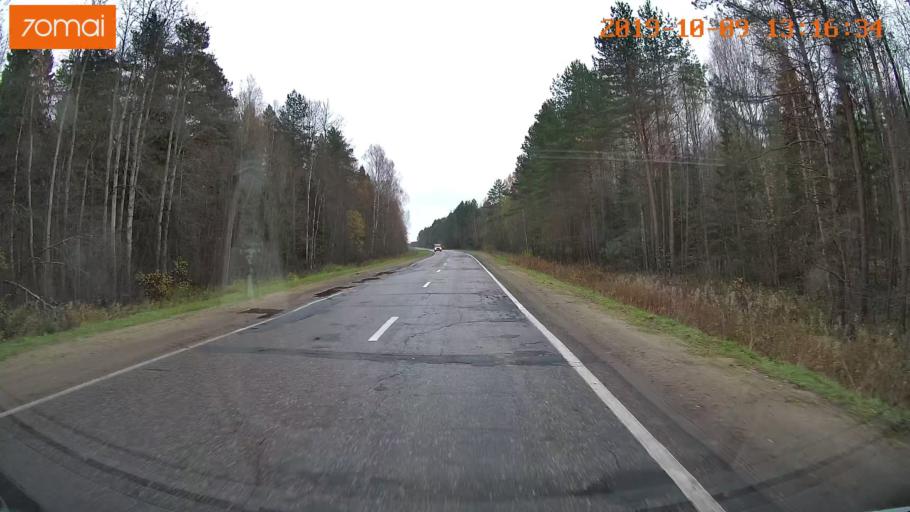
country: RU
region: Jaroslavl
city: Lyubim
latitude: 58.3602
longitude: 40.7677
